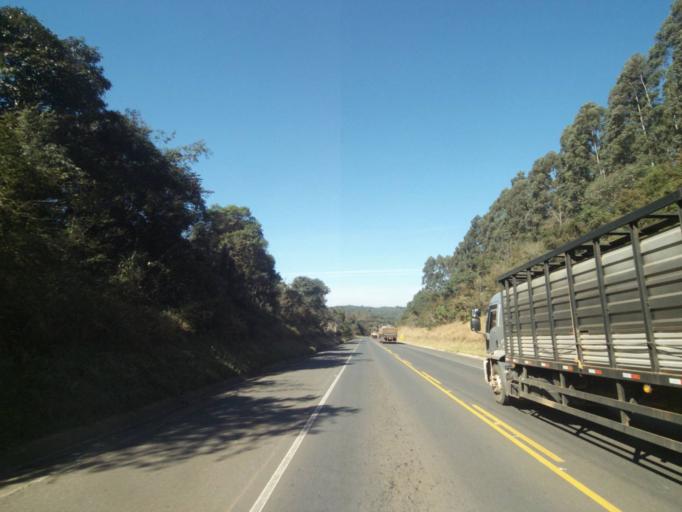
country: BR
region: Parana
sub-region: Tibagi
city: Tibagi
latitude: -24.5661
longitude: -50.4536
